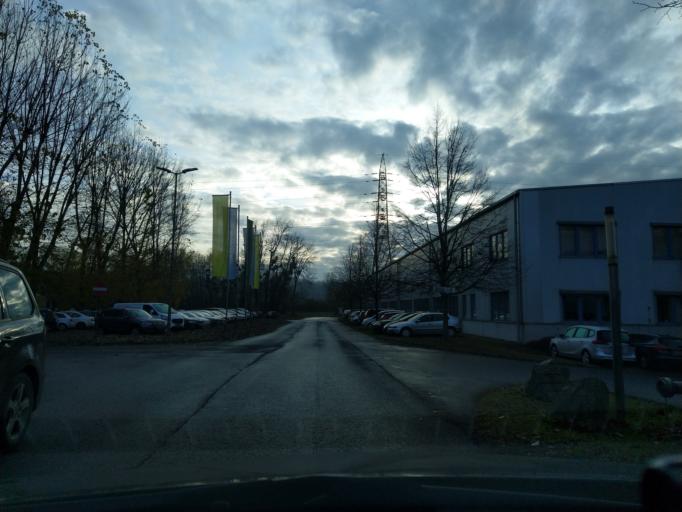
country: AT
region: Upper Austria
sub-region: Politischer Bezirk Urfahr-Umgebung
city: Steyregg
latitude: 48.2644
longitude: 14.3408
